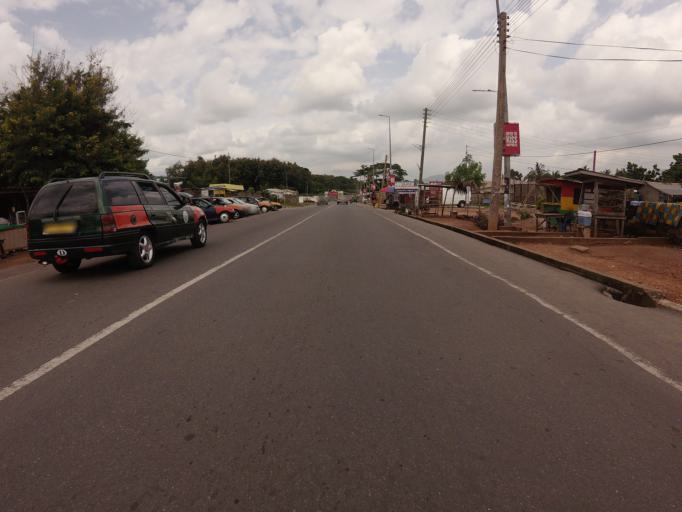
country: GH
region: Volta
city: Ho
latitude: 6.6009
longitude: 0.4716
